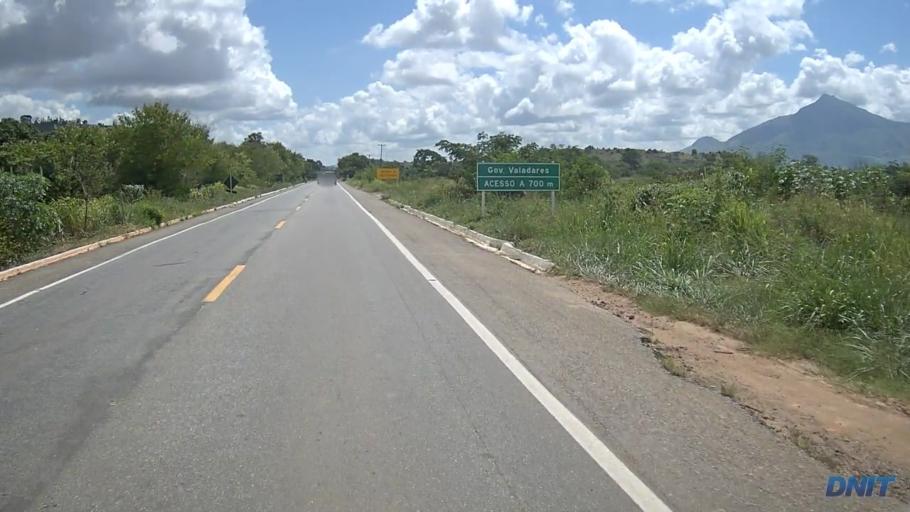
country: BR
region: Minas Gerais
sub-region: Governador Valadares
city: Governador Valadares
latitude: -18.9201
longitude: -42.0152
